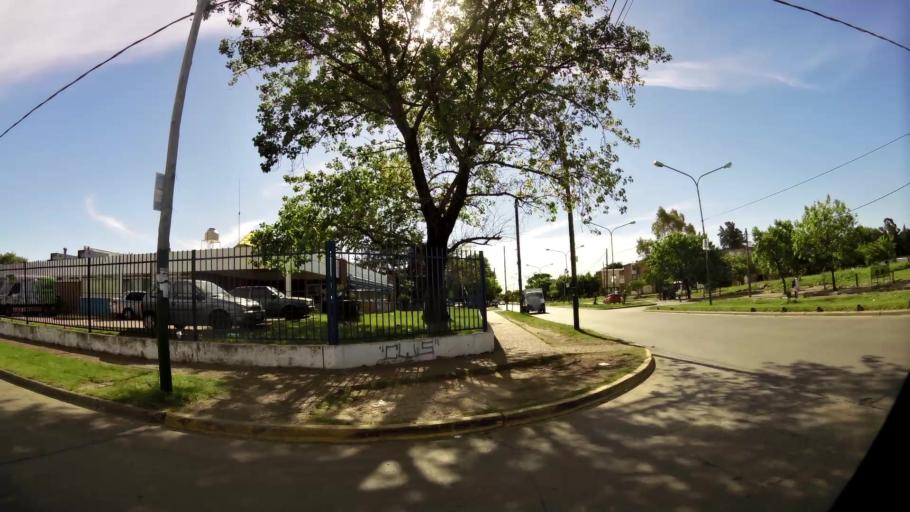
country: AR
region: Buenos Aires
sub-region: Partido de Almirante Brown
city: Adrogue
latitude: -34.8183
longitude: -58.3464
